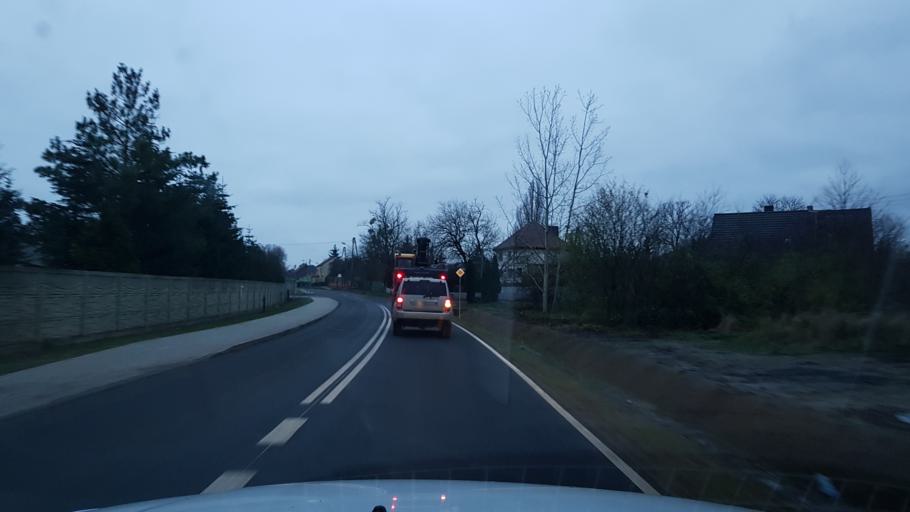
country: PL
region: West Pomeranian Voivodeship
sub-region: Powiat policki
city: Przeclaw
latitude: 53.4135
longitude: 14.4360
